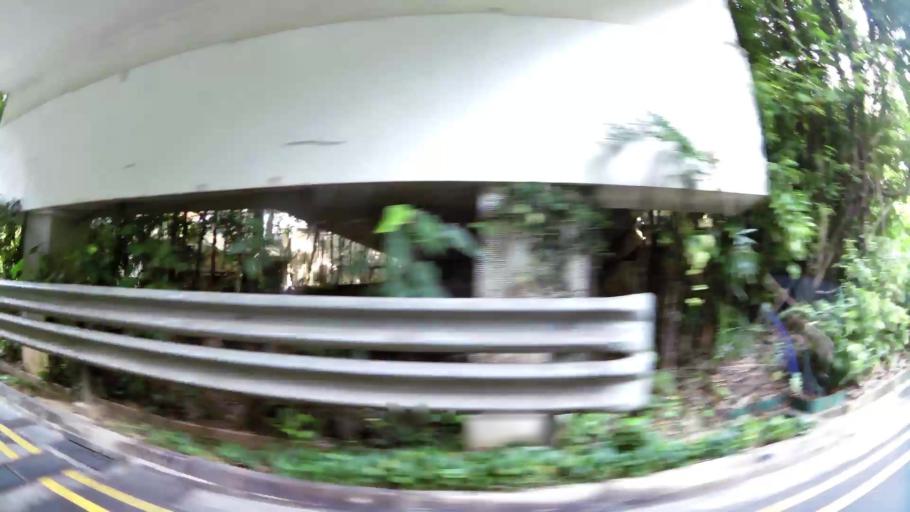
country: SG
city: Singapore
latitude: 1.2516
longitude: 103.8193
